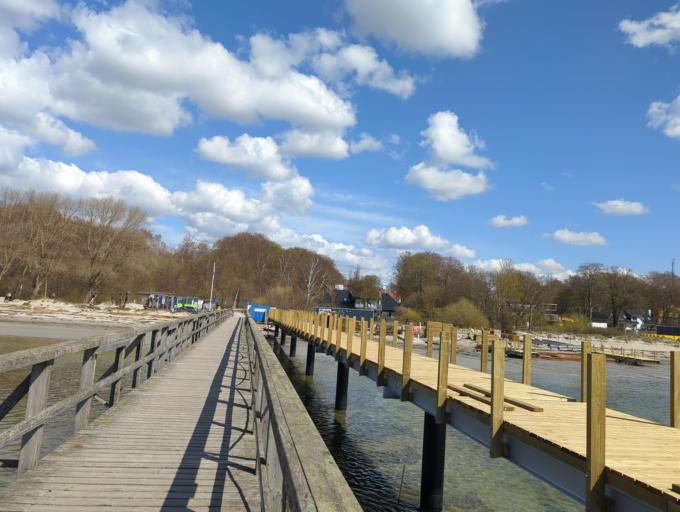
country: SE
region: Skane
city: Bjarred
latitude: 55.7114
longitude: 13.0224
